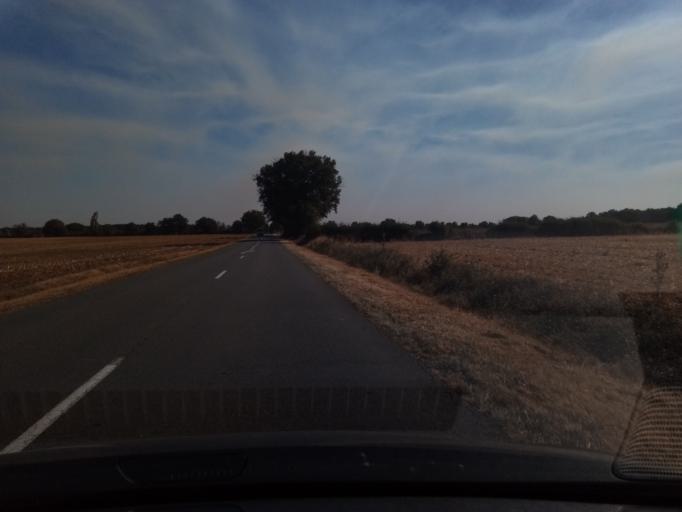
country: FR
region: Poitou-Charentes
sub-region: Departement de la Vienne
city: Montmorillon
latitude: 46.4917
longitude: 0.7843
